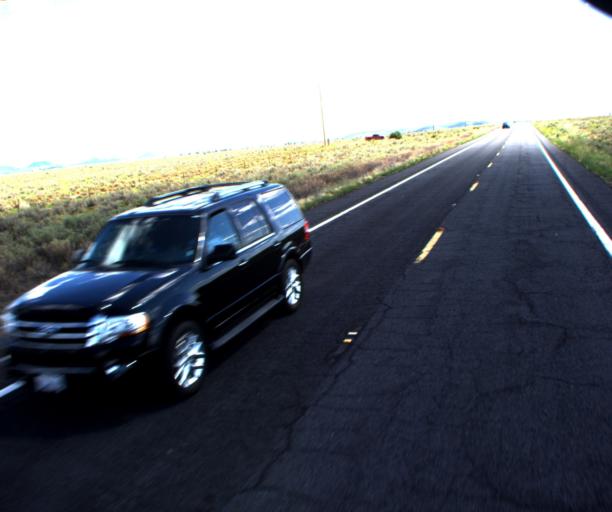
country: US
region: Arizona
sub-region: Coconino County
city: Williams
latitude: 35.6155
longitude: -112.1445
